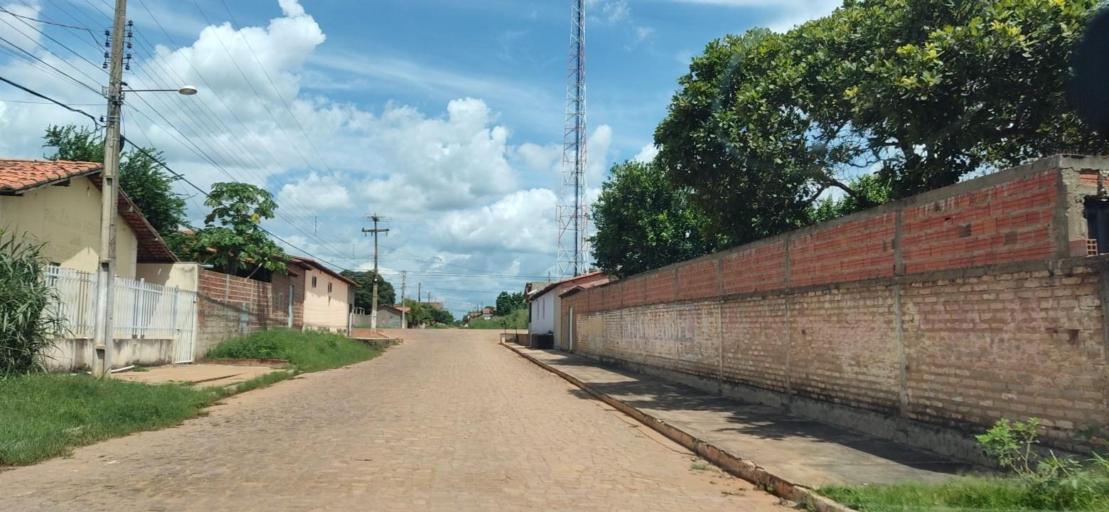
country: BR
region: Piaui
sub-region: Valenca Do Piaui
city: Valenca do Piaui
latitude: -6.4122
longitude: -41.7418
